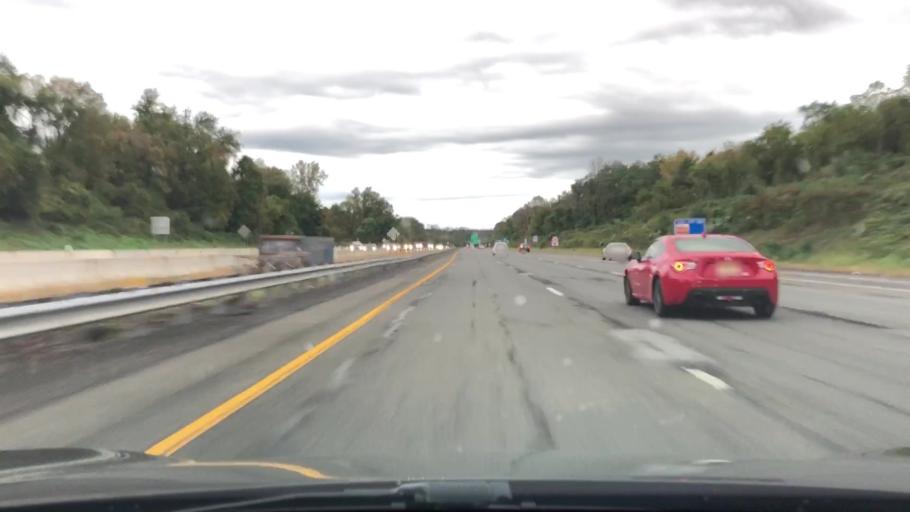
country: US
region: New Jersey
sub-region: Mercer County
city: Ewing
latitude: 40.2791
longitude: -74.8253
